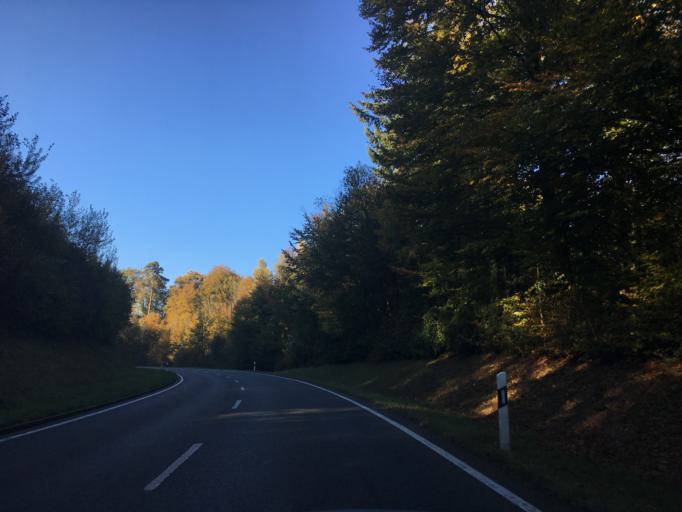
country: DE
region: Baden-Wuerttemberg
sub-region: Freiburg Region
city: Konstanz
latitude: 47.7054
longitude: 9.1728
